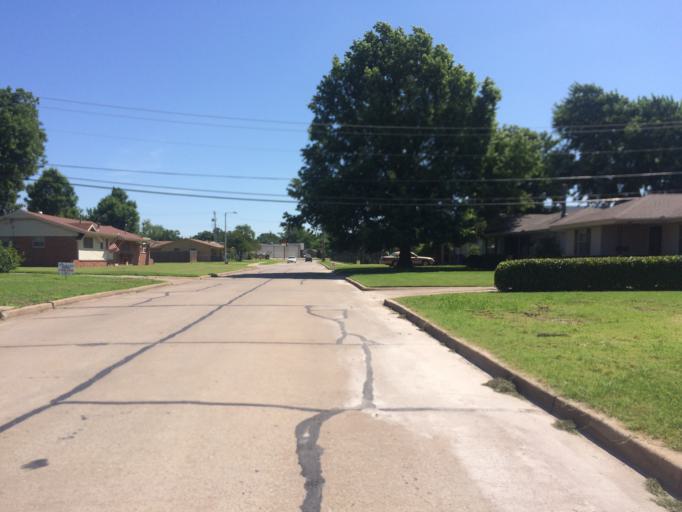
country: US
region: Oklahoma
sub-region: Cleveland County
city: Norman
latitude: 35.2269
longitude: -97.4613
